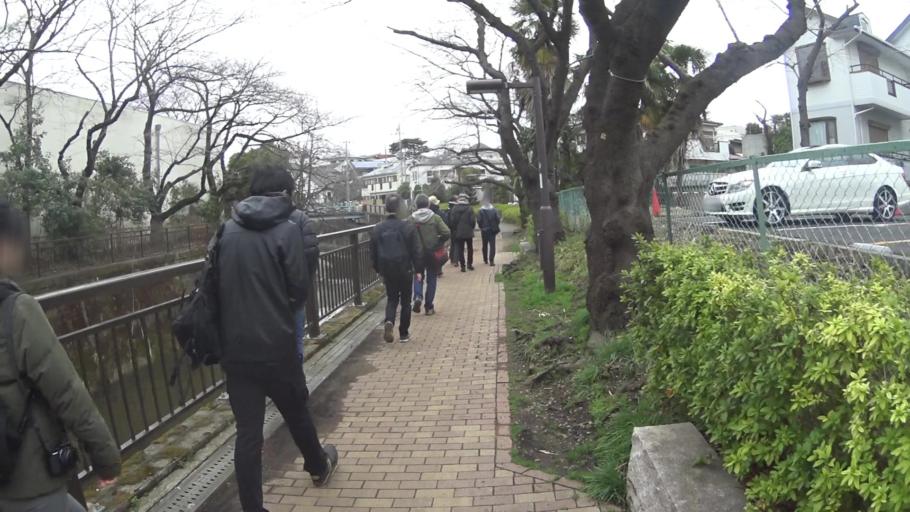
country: JP
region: Tokyo
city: Chofugaoka
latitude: 35.6374
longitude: 139.6043
